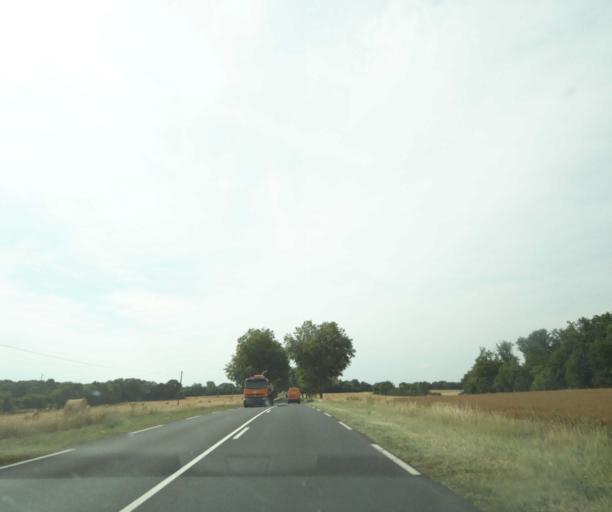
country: FR
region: Centre
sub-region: Departement d'Indre-et-Loire
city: Neuille-Pont-Pierre
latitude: 47.5213
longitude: 0.5818
